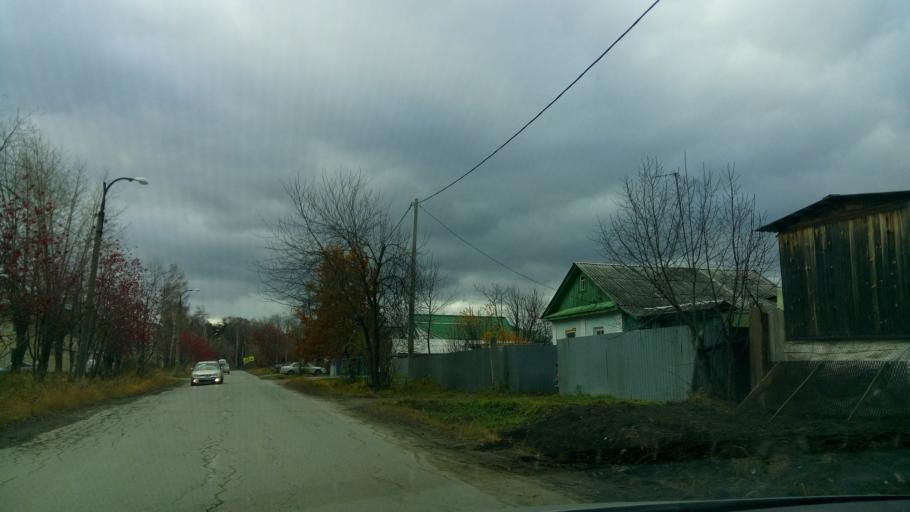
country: RU
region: Sverdlovsk
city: Sredneuralsk
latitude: 56.9918
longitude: 60.4733
